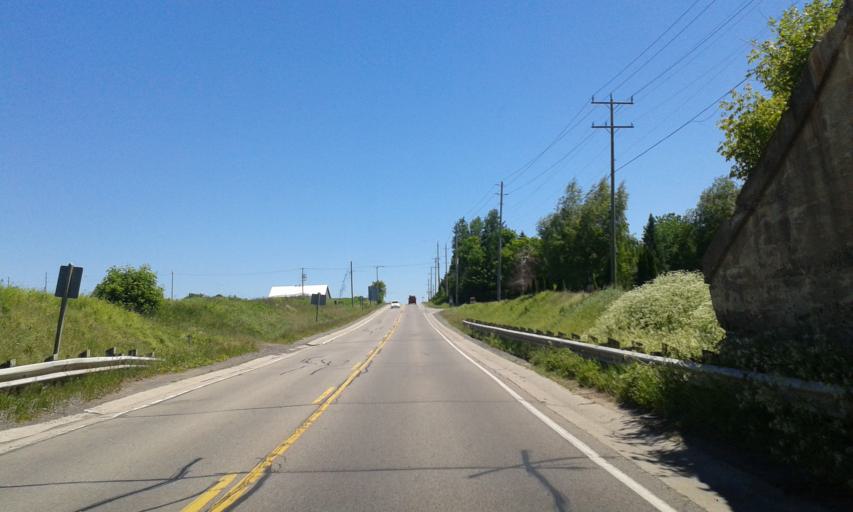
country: CA
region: Ontario
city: Prescott
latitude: 44.7208
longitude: -75.4928
